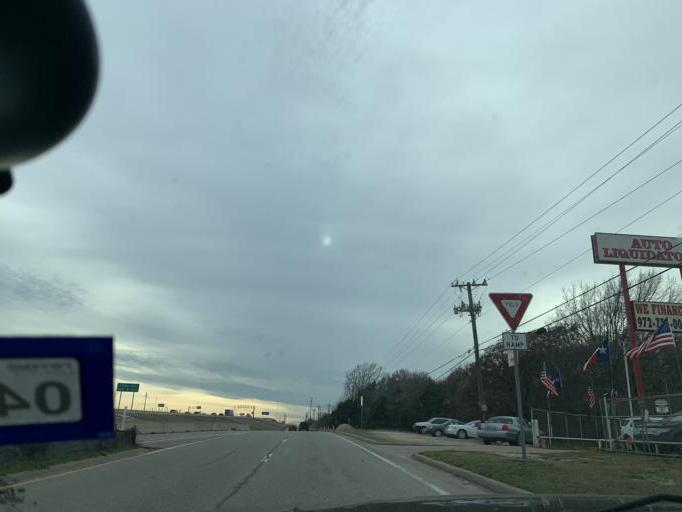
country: US
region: Texas
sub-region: Dallas County
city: Duncanville
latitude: 32.6234
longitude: -96.9110
